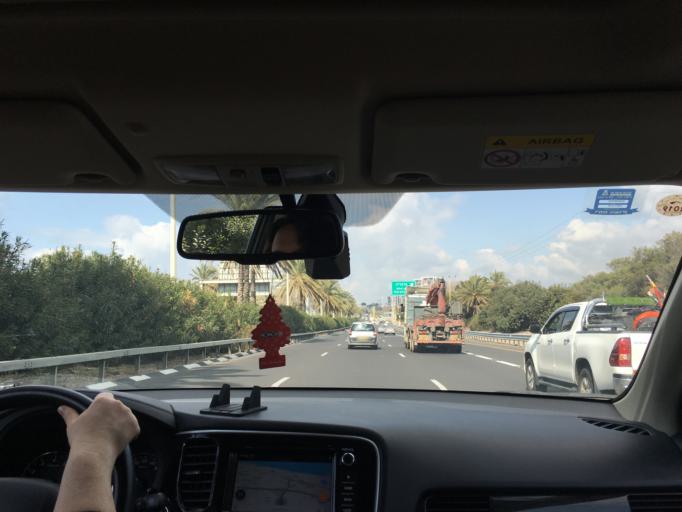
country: IL
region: Tel Aviv
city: Herzliya Pituah
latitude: 32.1526
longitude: 34.8064
